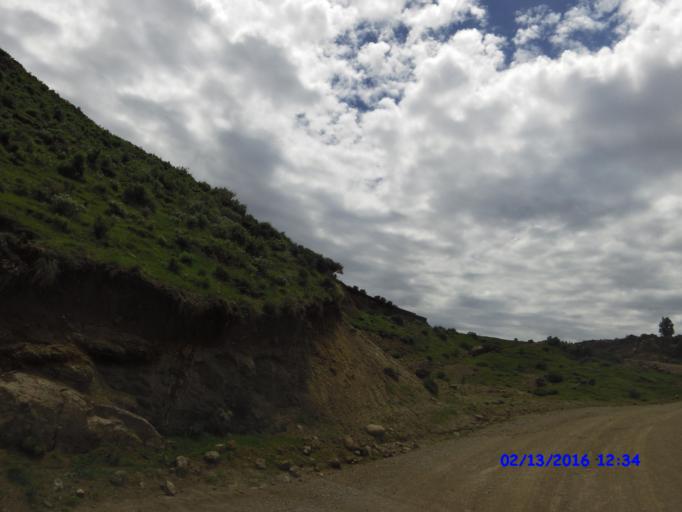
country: LS
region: Maseru
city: Nako
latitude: -29.8480
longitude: 28.0274
